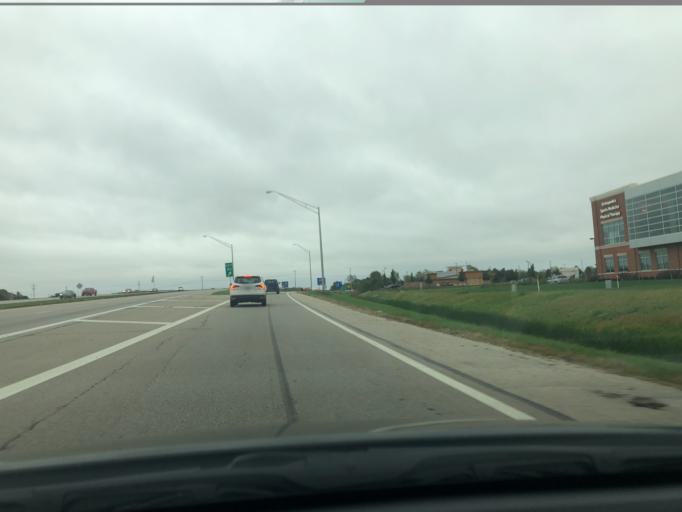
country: US
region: Ohio
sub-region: Union County
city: Marysville
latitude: 40.2418
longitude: -83.3492
